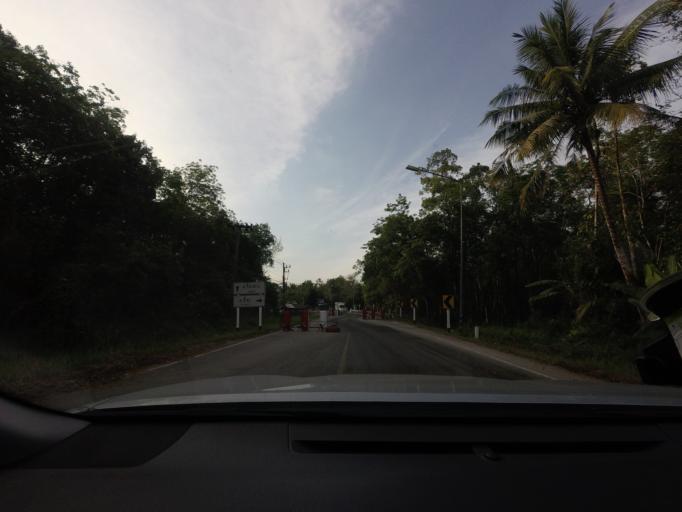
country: TH
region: Narathiwat
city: Ra-ngae
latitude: 6.3366
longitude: 101.7200
